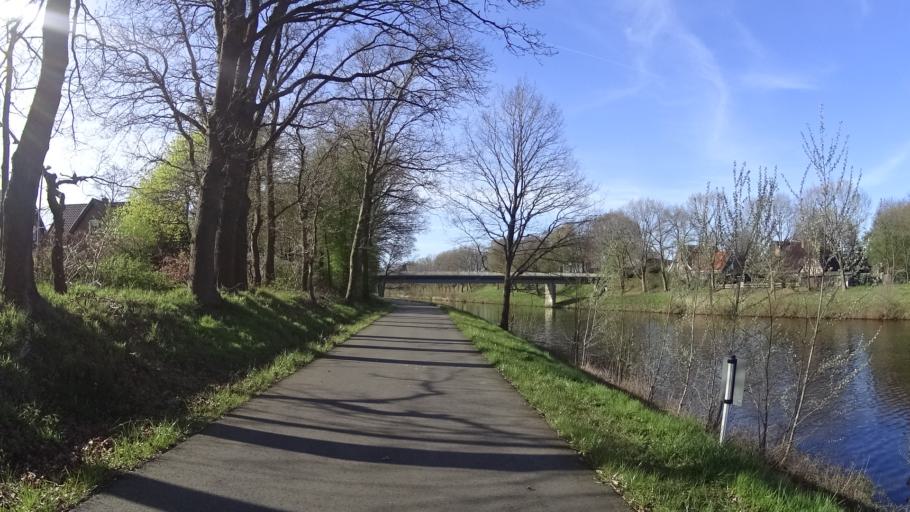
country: DE
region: Lower Saxony
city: Haren
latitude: 52.7494
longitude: 7.2603
